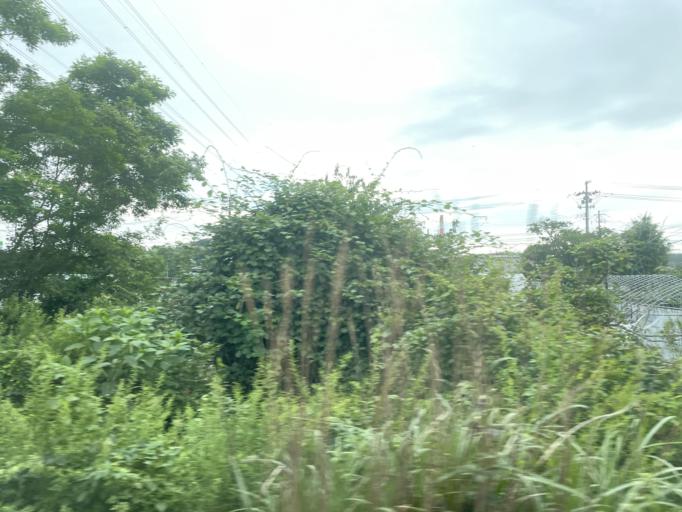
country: JP
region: Akita
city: Akita Shi
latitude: 39.7859
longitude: 140.0661
